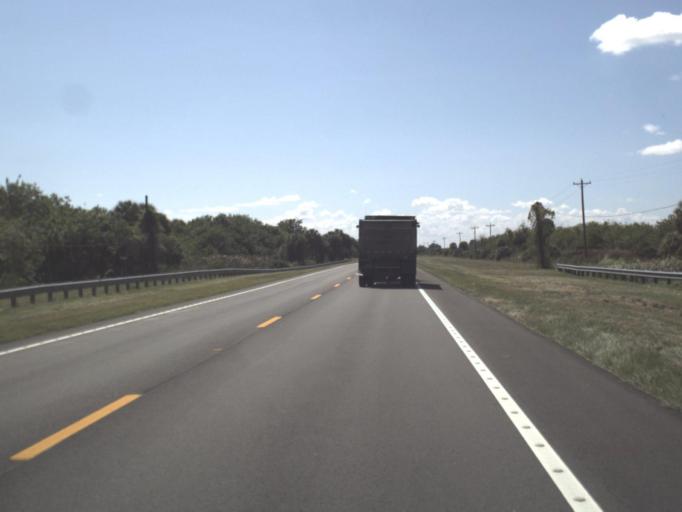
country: US
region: Florida
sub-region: Glades County
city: Buckhead Ridge
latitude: 27.0292
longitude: -81.0087
